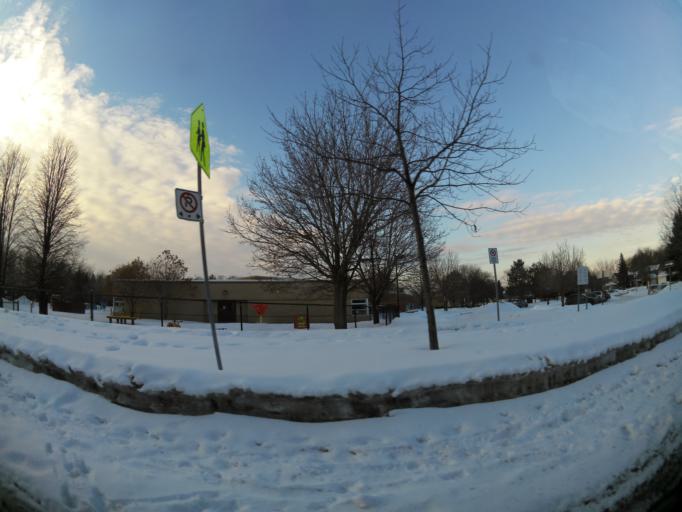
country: CA
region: Ontario
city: Ottawa
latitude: 45.4490
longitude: -75.5372
